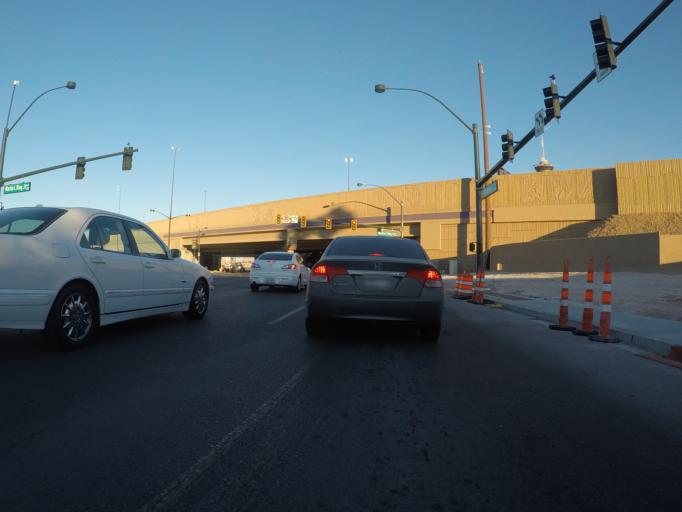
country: US
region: Nevada
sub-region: Clark County
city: Las Vegas
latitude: 36.1514
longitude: -115.1660
